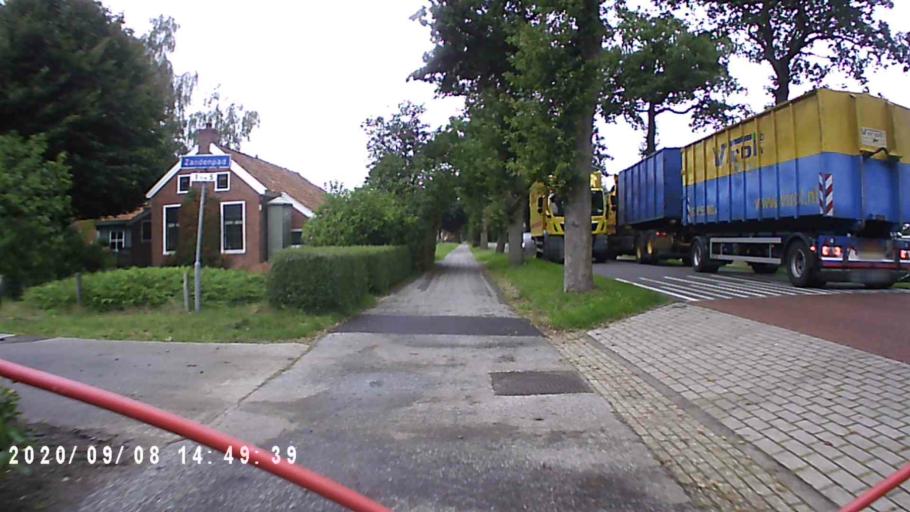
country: NL
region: Groningen
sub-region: Gemeente Slochteren
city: Slochteren
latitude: 53.2425
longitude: 6.8026
